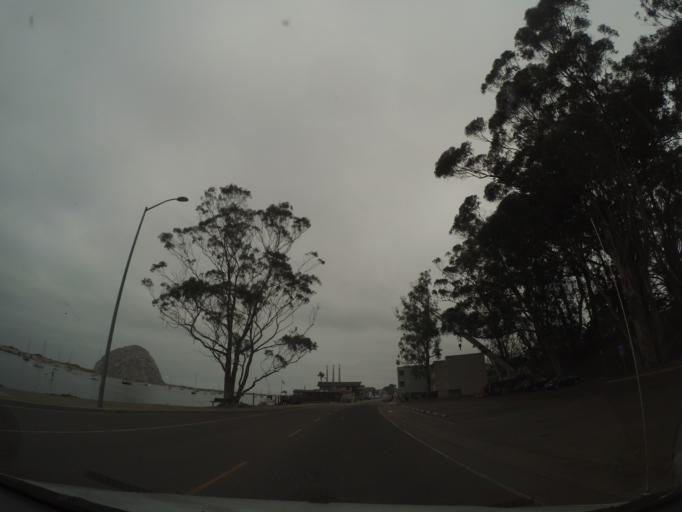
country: US
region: California
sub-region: San Luis Obispo County
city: Morro Bay
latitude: 35.3609
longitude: -120.8518
